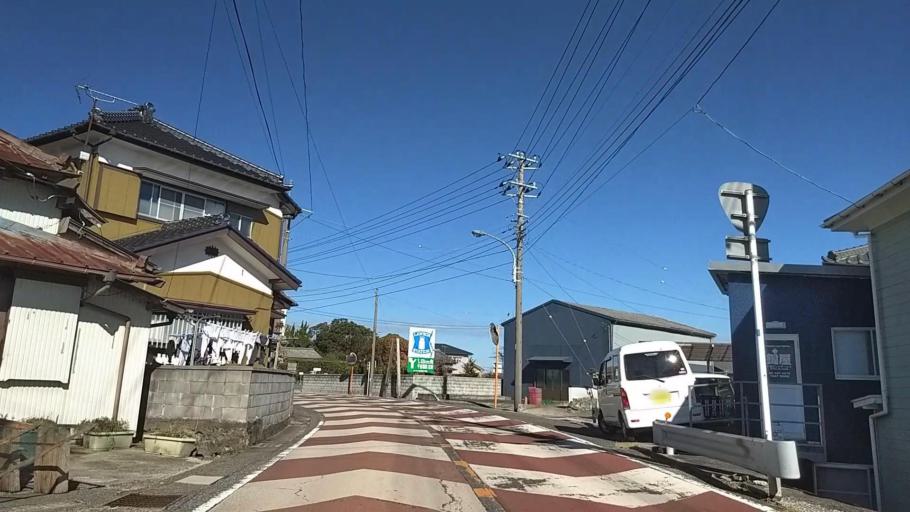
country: JP
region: Chiba
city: Tateyama
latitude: 34.9480
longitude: 139.9630
